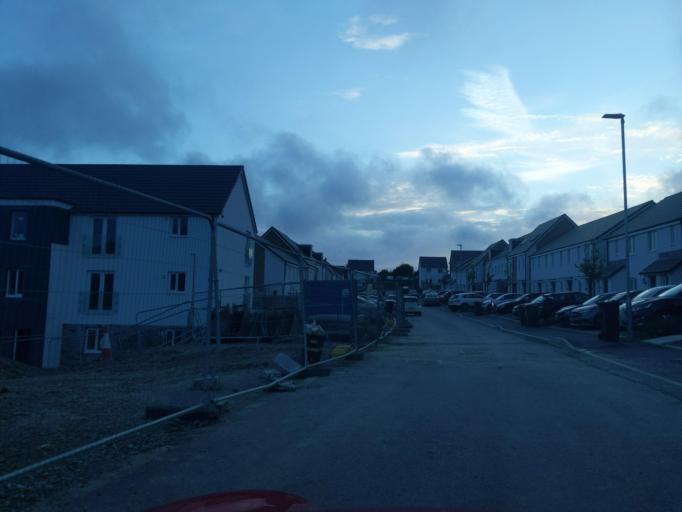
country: GB
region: England
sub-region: Plymouth
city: Plymouth
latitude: 50.4099
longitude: -4.1196
